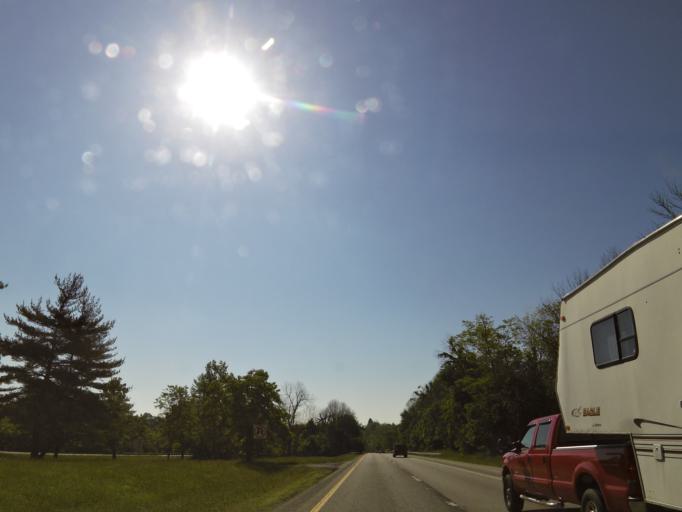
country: US
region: Kentucky
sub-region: Shelby County
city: Shelbyville
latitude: 38.1825
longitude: -85.1875
